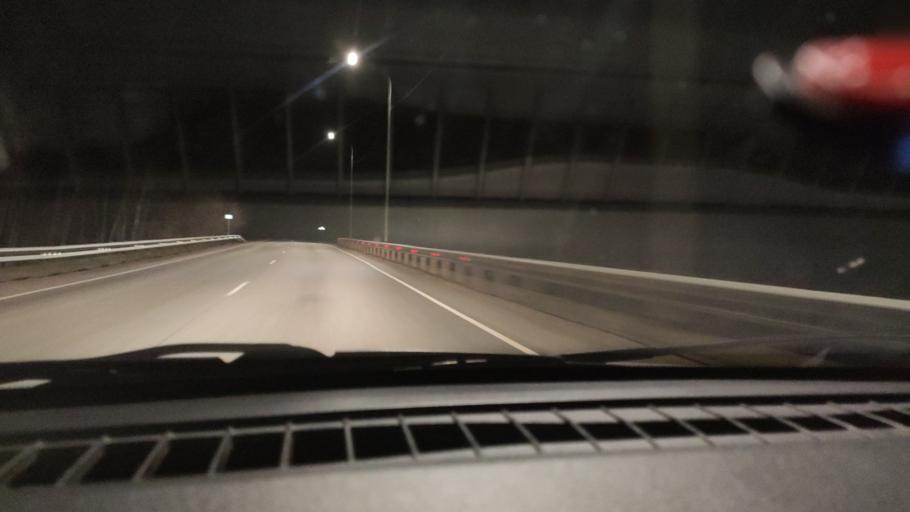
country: RU
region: Bashkortostan
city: Yermolayevo
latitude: 52.6541
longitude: 55.8354
